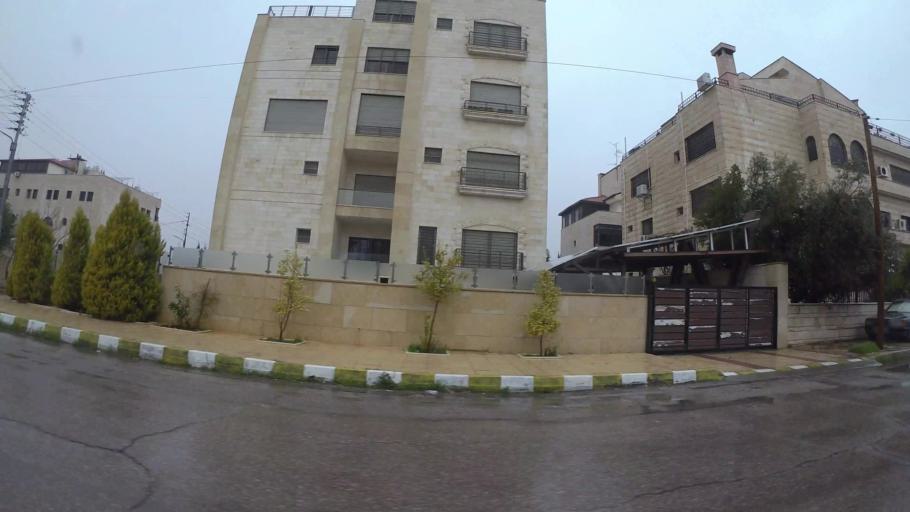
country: JO
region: Amman
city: Wadi as Sir
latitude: 31.9655
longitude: 35.8704
